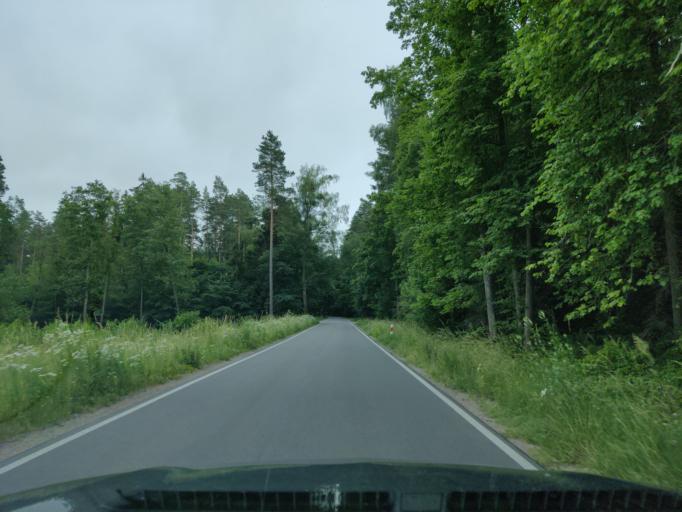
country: PL
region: Warmian-Masurian Voivodeship
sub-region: Powiat gizycki
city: Ryn
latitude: 53.8845
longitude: 21.5778
